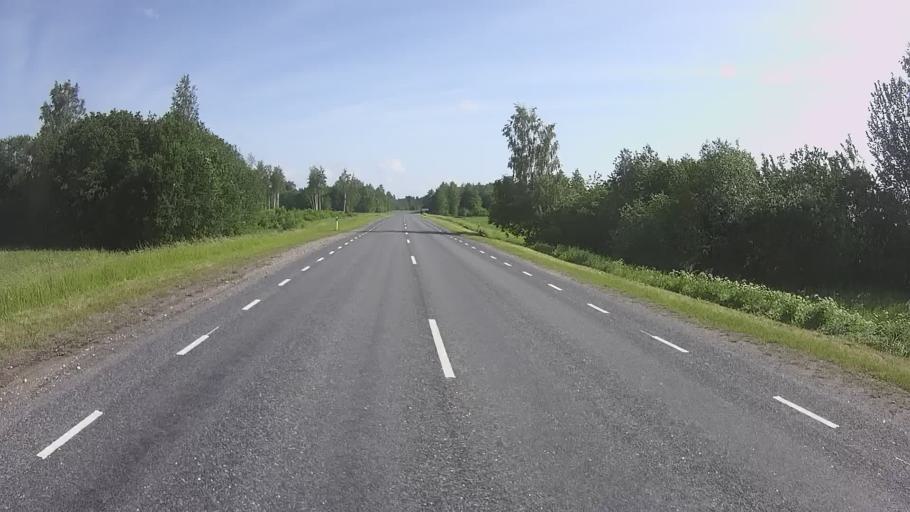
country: EE
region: Valgamaa
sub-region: Torva linn
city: Torva
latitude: 58.0177
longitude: 25.9486
